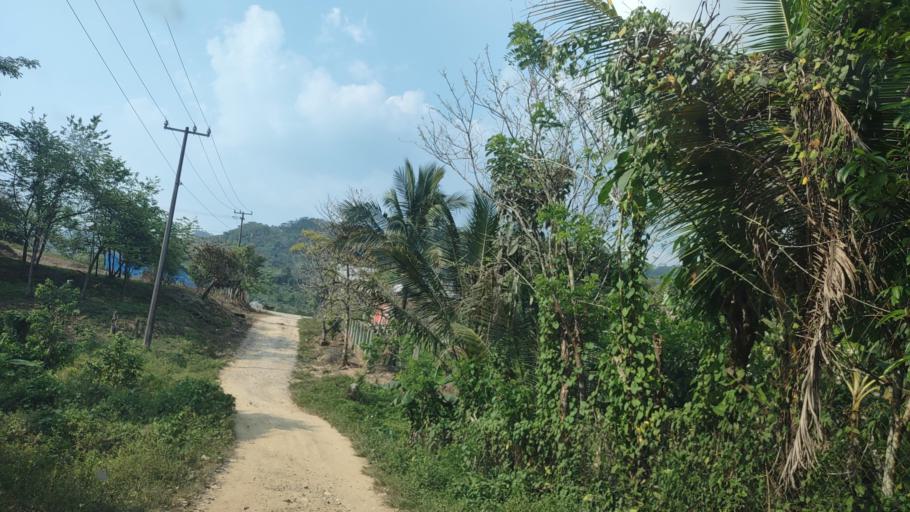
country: MX
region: Chiapas
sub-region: Tecpatan
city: Raudales Malpaso
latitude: 17.3229
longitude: -93.7462
